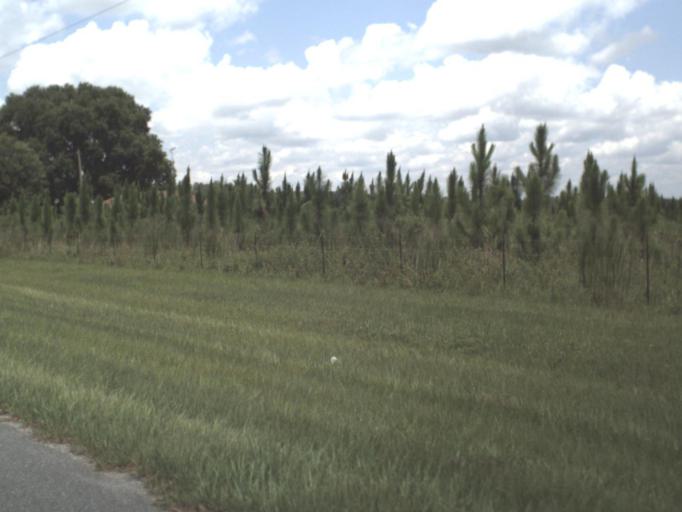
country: US
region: Florida
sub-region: Union County
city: Lake Butler
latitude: 30.0209
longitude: -82.3731
